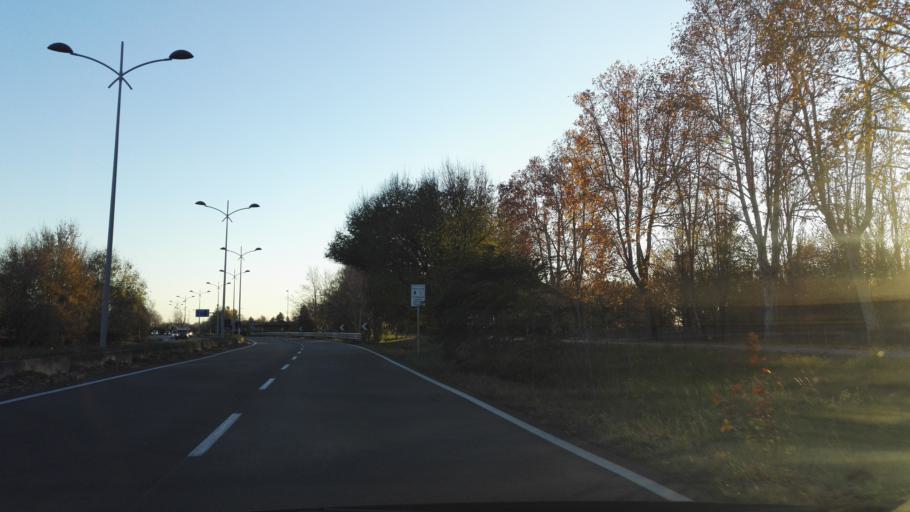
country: IT
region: Lombardy
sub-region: Citta metropolitana di Milano
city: Novegro-Tregarezzo-San Felice
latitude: 45.4705
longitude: 9.2948
